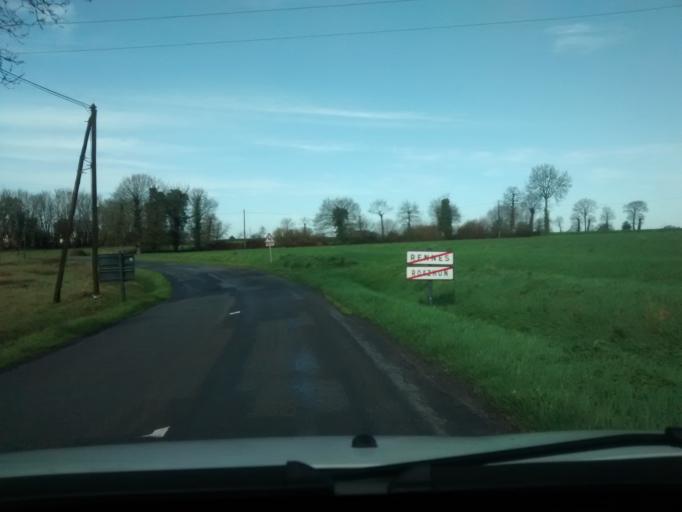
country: FR
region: Brittany
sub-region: Departement d'Ille-et-Vilaine
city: Montgermont
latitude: 48.1399
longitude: -1.7281
